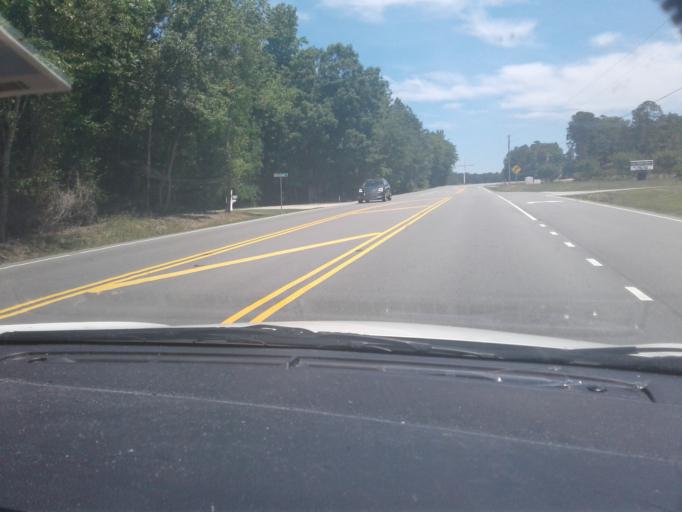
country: US
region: North Carolina
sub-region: Harnett County
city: Lillington
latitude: 35.4720
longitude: -78.8270
